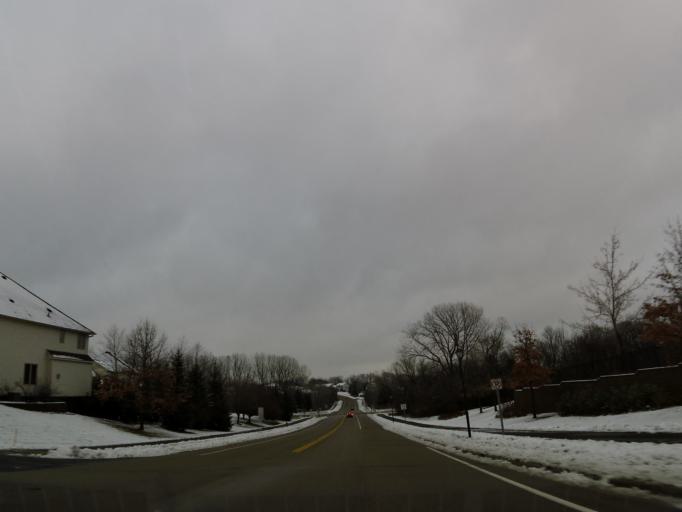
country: US
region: Minnesota
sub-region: Dakota County
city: Apple Valley
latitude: 44.7102
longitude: -93.2404
